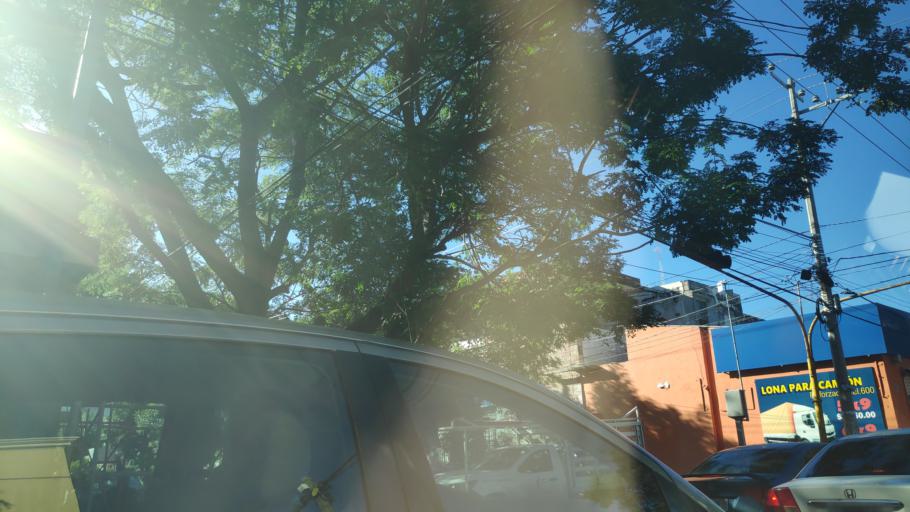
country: MX
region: Sinaloa
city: Culiacan
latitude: 24.8091
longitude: -107.4043
